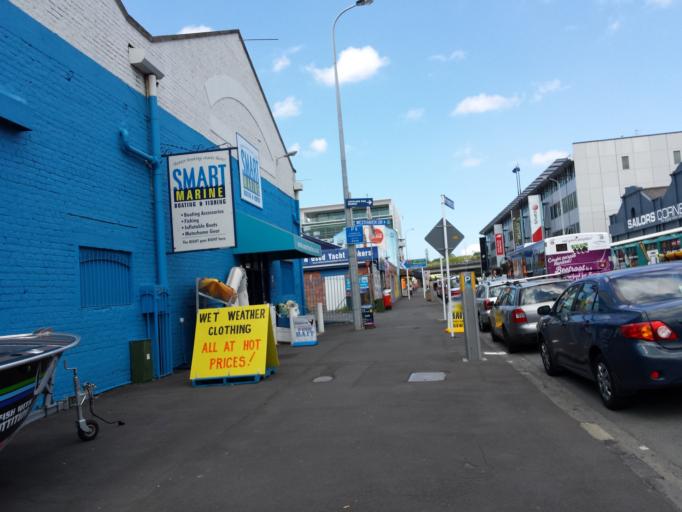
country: NZ
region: Auckland
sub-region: Auckland
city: Auckland
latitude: -36.8432
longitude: 174.7538
